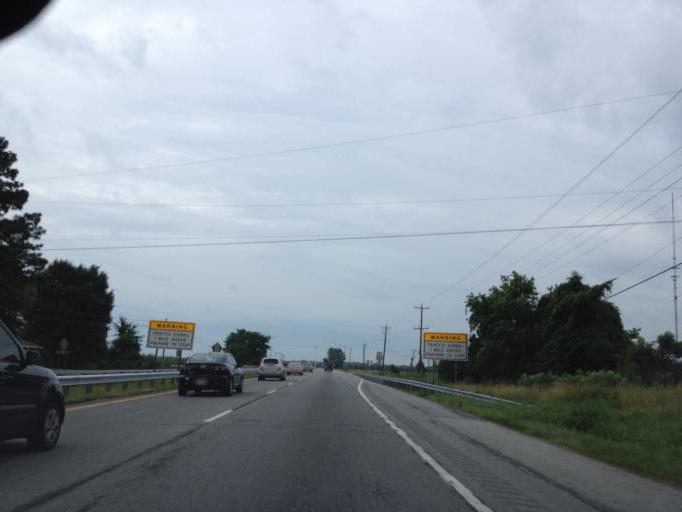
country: US
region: Maryland
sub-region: Queen Anne's County
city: Centreville
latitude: 38.9602
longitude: -76.0959
